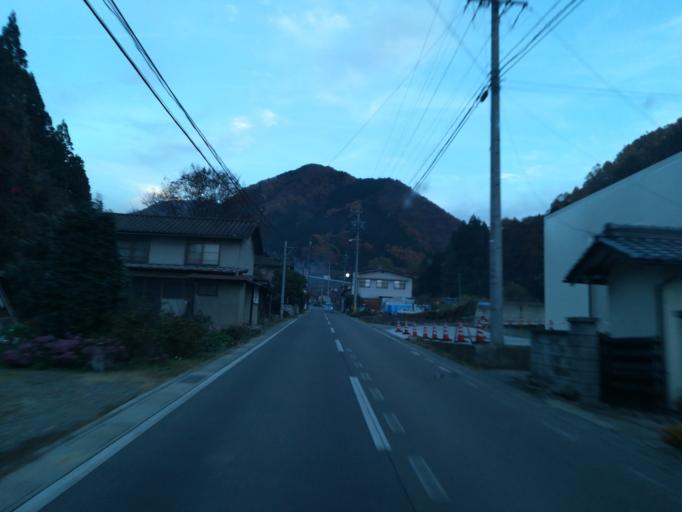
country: JP
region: Nagano
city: Suzaka
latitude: 36.5830
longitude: 138.2756
